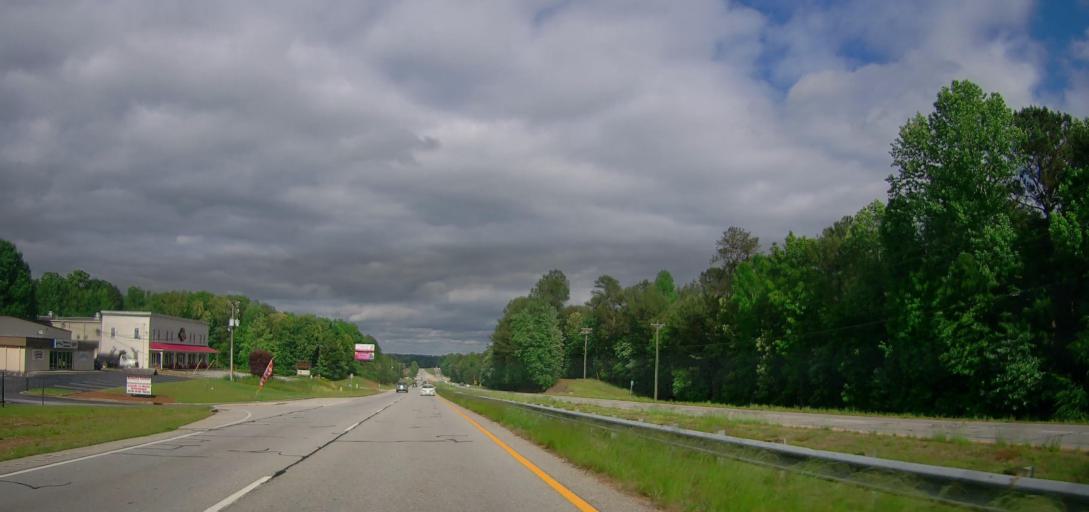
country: US
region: Georgia
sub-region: Walton County
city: Monroe
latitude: 33.8058
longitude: -83.7834
